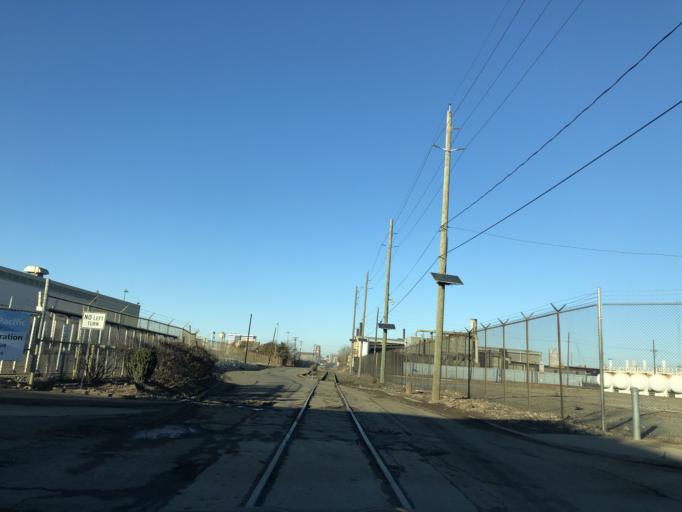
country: US
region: New Jersey
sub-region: Camden County
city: Camden
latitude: 39.9316
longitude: -75.1292
